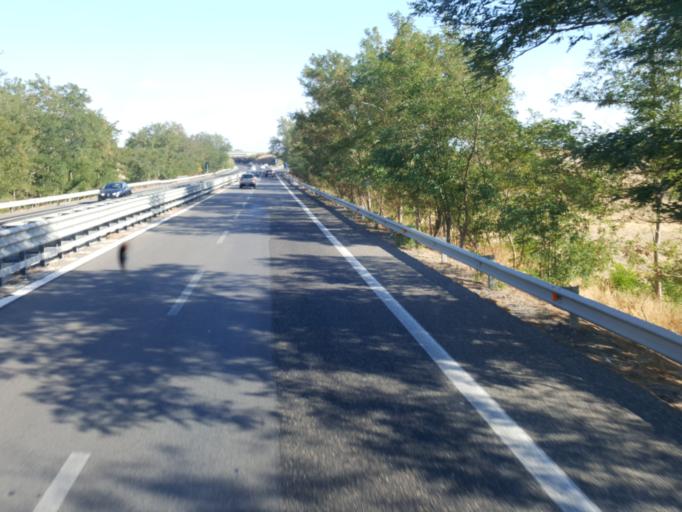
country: IT
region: Latium
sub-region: Provincia di Viterbo
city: Montalto di Castro
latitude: 42.3737
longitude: 11.5593
